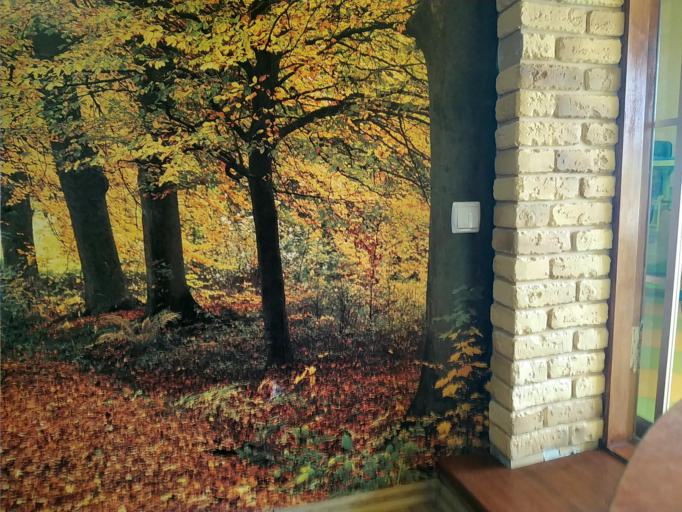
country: RU
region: Smolensk
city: Safonovo
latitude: 55.1072
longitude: 33.1419
